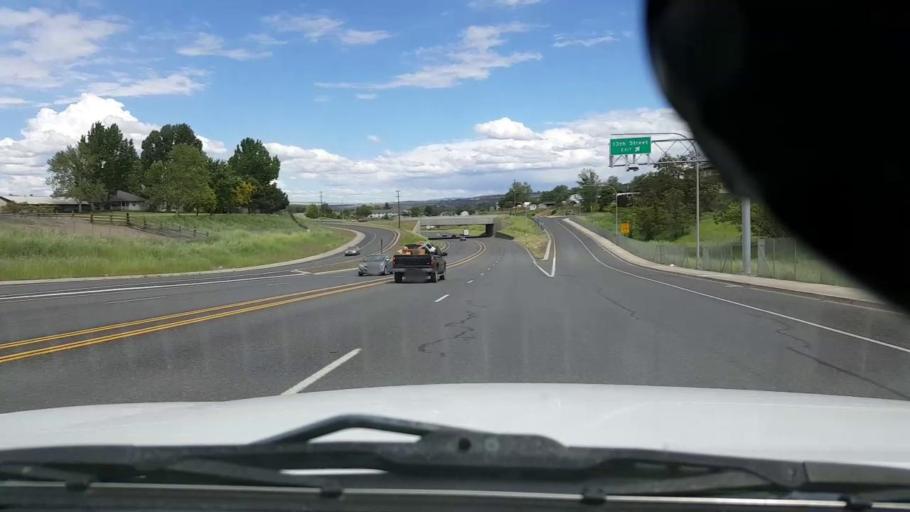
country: US
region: Washington
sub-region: Asotin County
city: West Clarkston-Highland
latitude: 46.4012
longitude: -117.0645
